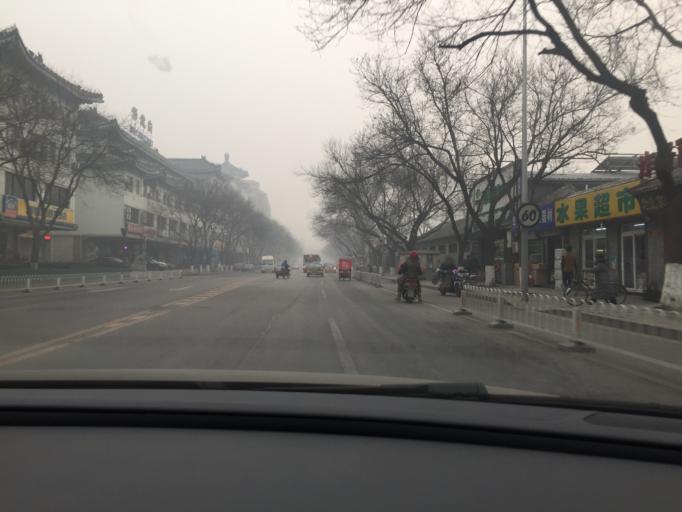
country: CN
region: Beijing
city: Beijing
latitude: 39.9103
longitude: 116.4006
